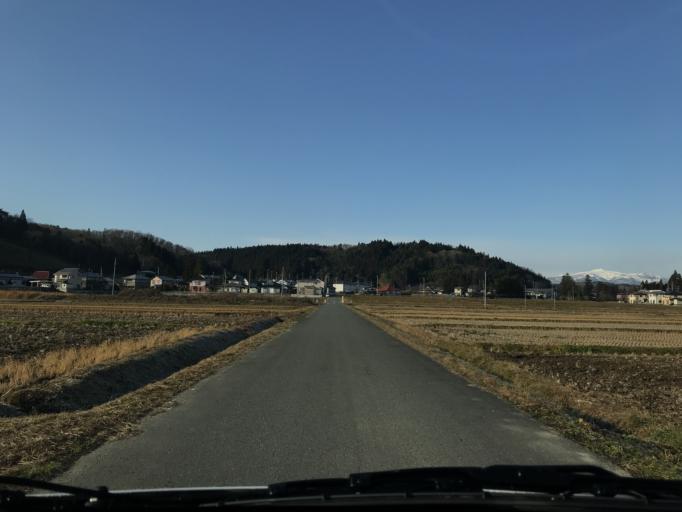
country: JP
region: Iwate
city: Ichinoseki
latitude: 38.9169
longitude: 141.0969
